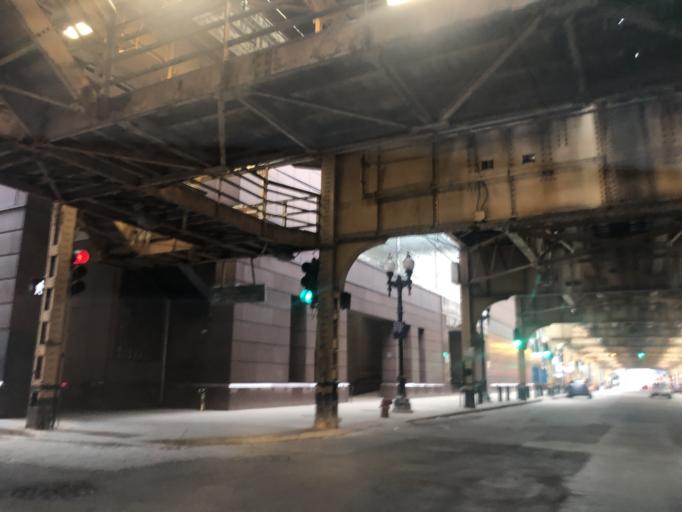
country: US
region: Illinois
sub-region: Cook County
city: Chicago
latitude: 41.8768
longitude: -87.6313
